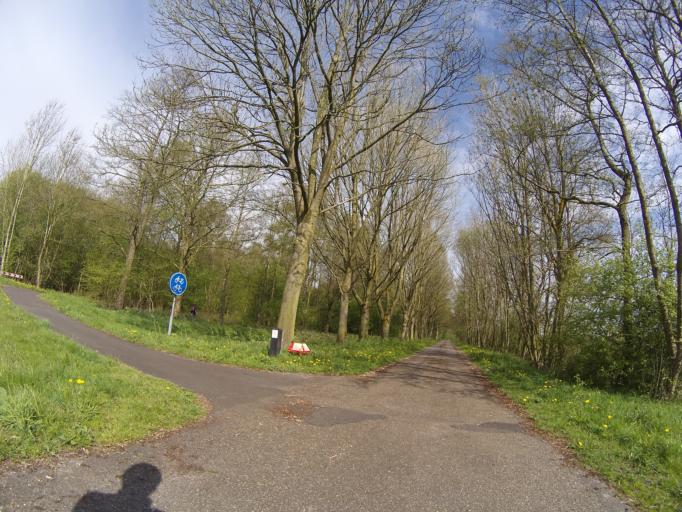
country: NL
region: Drenthe
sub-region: Gemeente Coevorden
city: Sleen
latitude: 52.8088
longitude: 6.6950
